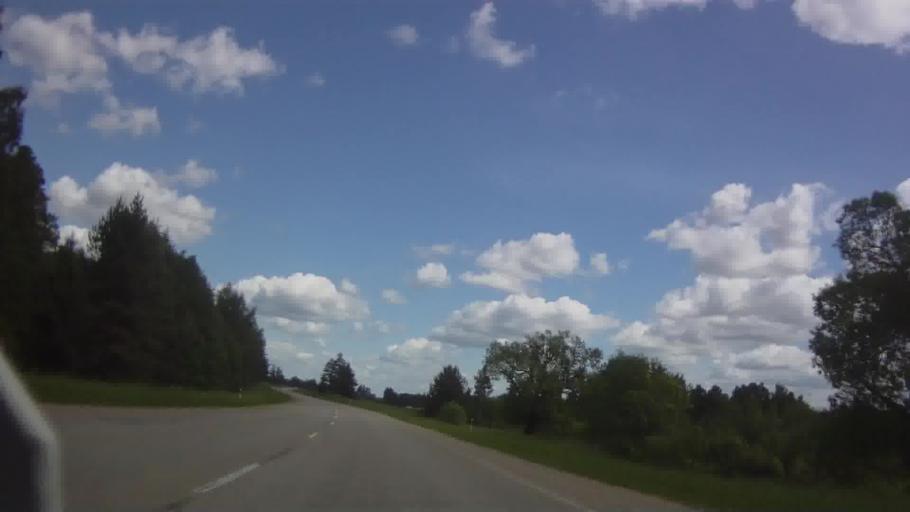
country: LV
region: Varaklani
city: Varaklani
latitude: 56.5880
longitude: 26.7087
